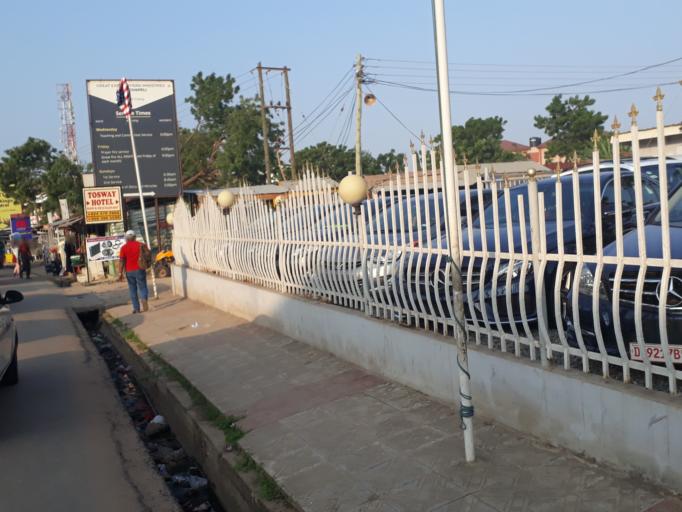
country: GH
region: Greater Accra
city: Dome
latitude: 5.6415
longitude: -0.2391
